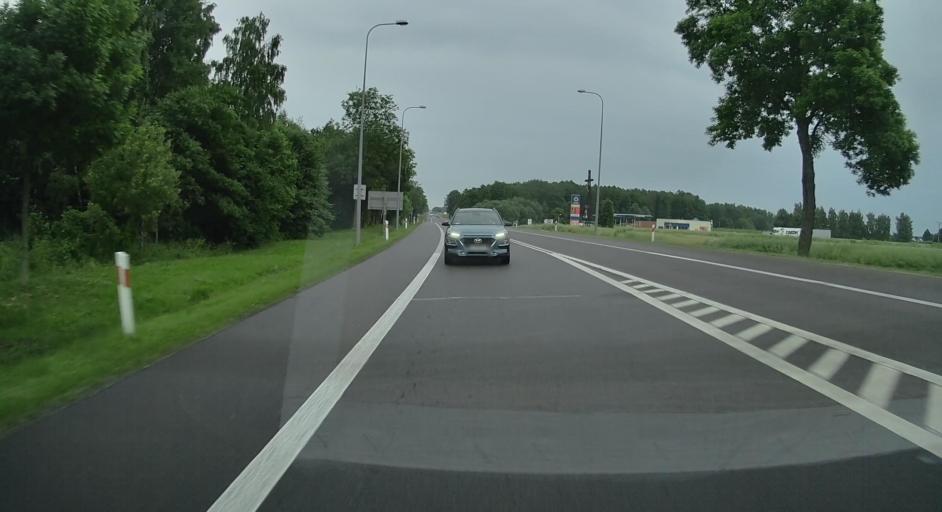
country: PL
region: Lublin Voivodeship
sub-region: Powiat bialski
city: Miedzyrzec Podlaski
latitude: 52.0009
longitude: 22.8166
